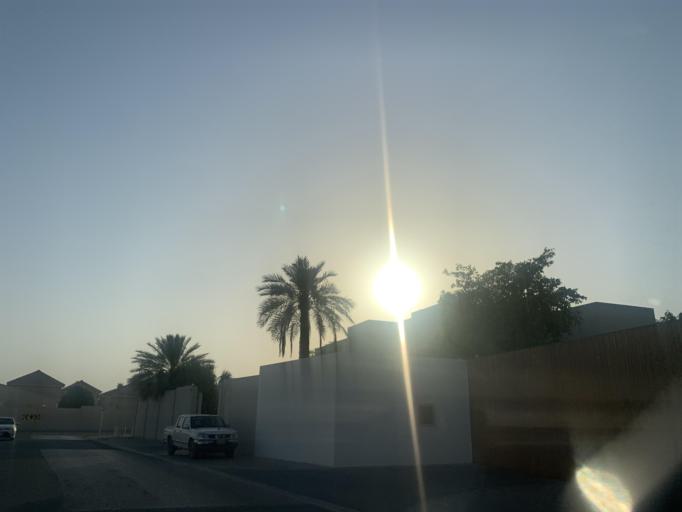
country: BH
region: Northern
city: Madinat `Isa
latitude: 26.1927
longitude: 50.4775
